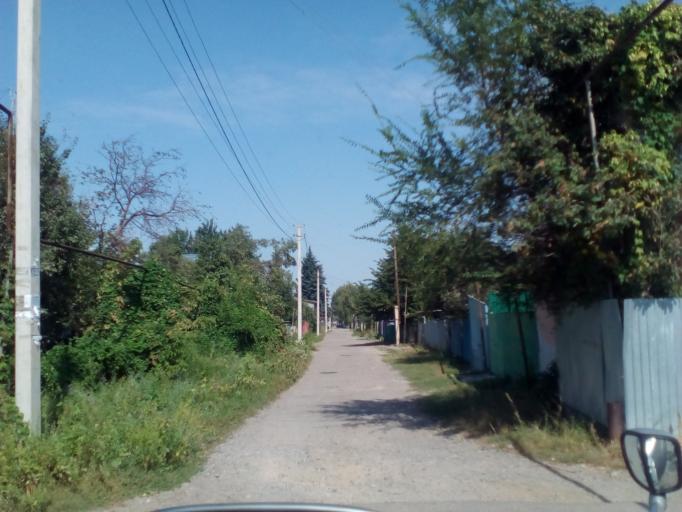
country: KZ
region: Almaty Oblysy
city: Burunday
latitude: 43.1588
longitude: 76.4078
